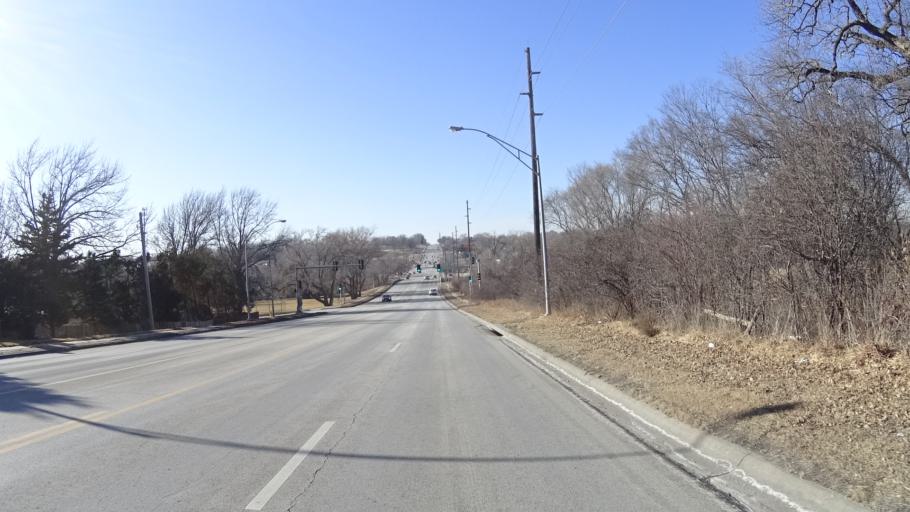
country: US
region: Nebraska
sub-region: Douglas County
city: Ralston
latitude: 41.3068
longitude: -96.0463
